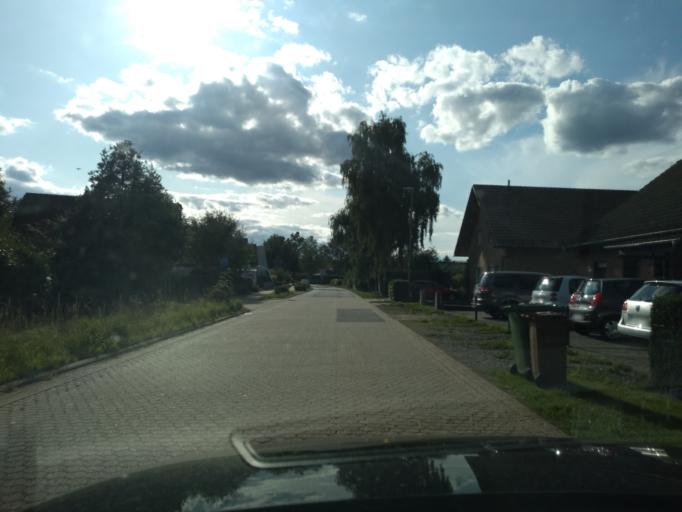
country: DE
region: North Rhine-Westphalia
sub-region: Regierungsbezirk Koln
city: Much
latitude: 50.8542
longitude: 7.3729
